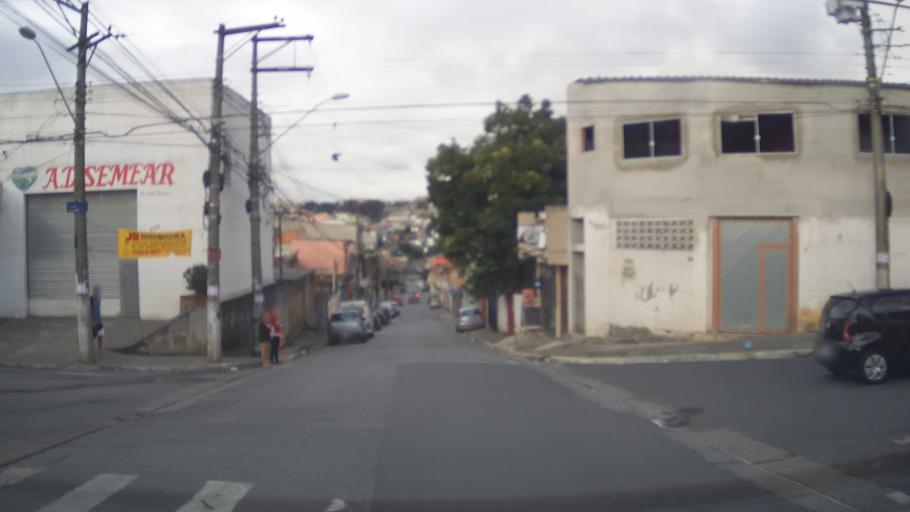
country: BR
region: Sao Paulo
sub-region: Itaquaquecetuba
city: Itaquaquecetuba
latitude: -23.4478
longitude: -46.4229
